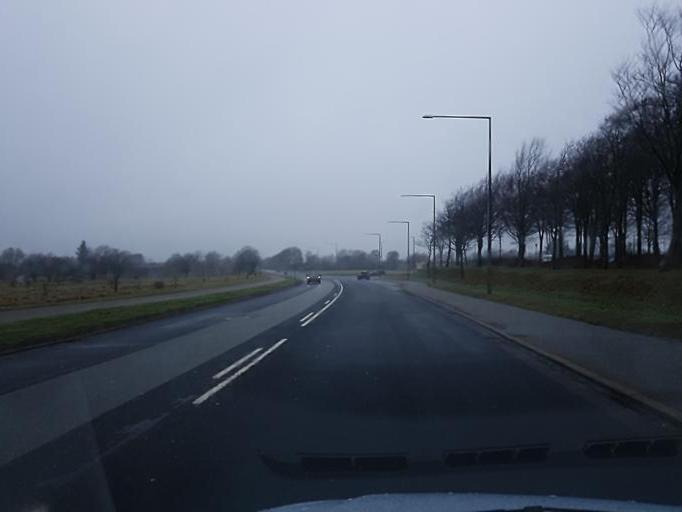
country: DK
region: South Denmark
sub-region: Esbjerg Kommune
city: Esbjerg
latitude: 55.4929
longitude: 8.4845
